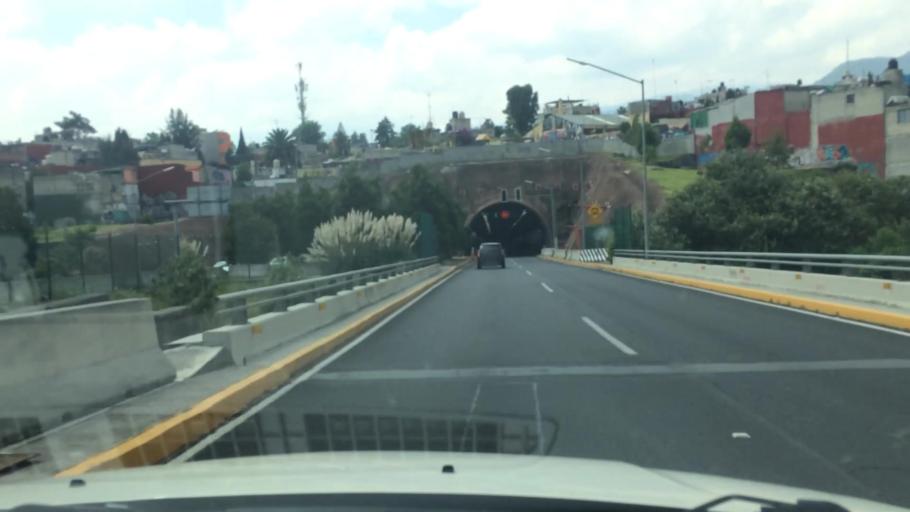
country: MX
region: Mexico City
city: Magdalena Contreras
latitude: 19.3247
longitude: -99.2396
